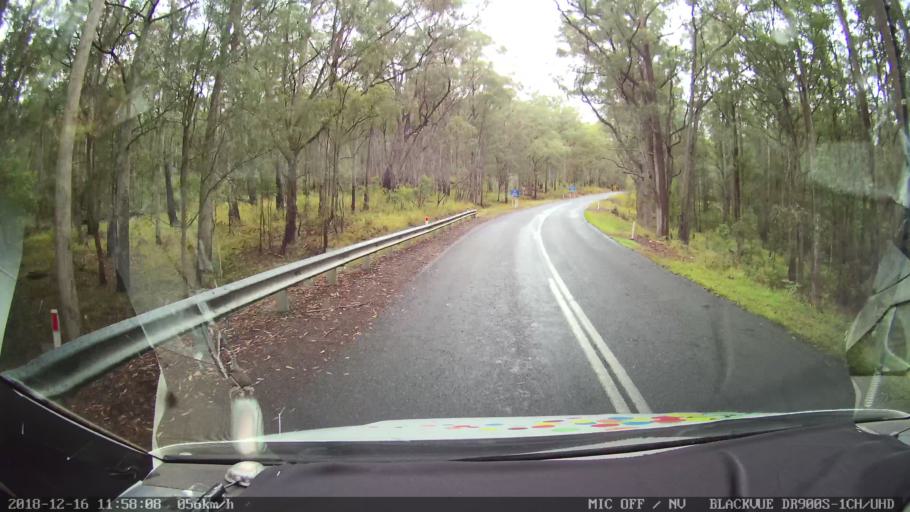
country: AU
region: New South Wales
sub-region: Tenterfield Municipality
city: Carrolls Creek
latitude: -28.9197
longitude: 152.3129
